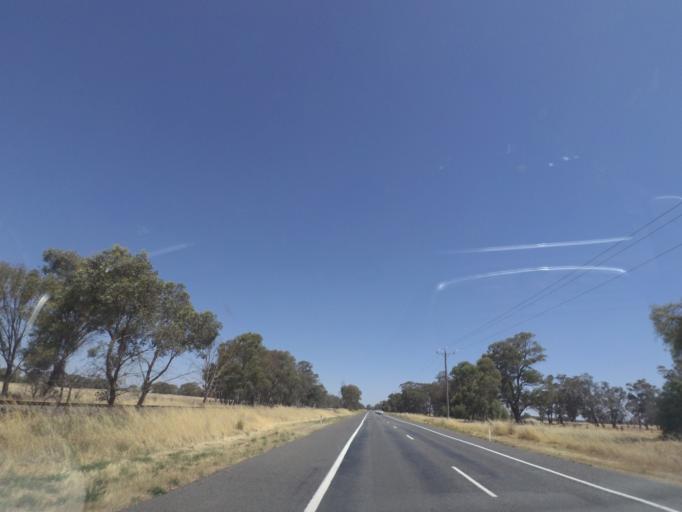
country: AU
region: Victoria
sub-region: Greater Shepparton
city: Shepparton
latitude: -36.2154
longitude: 145.4318
